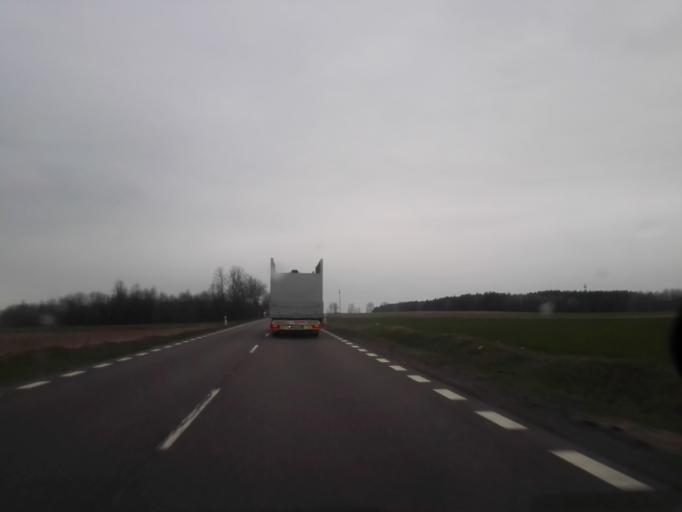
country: PL
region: Podlasie
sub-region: Powiat grajewski
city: Grajewo
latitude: 53.6086
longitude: 22.3738
